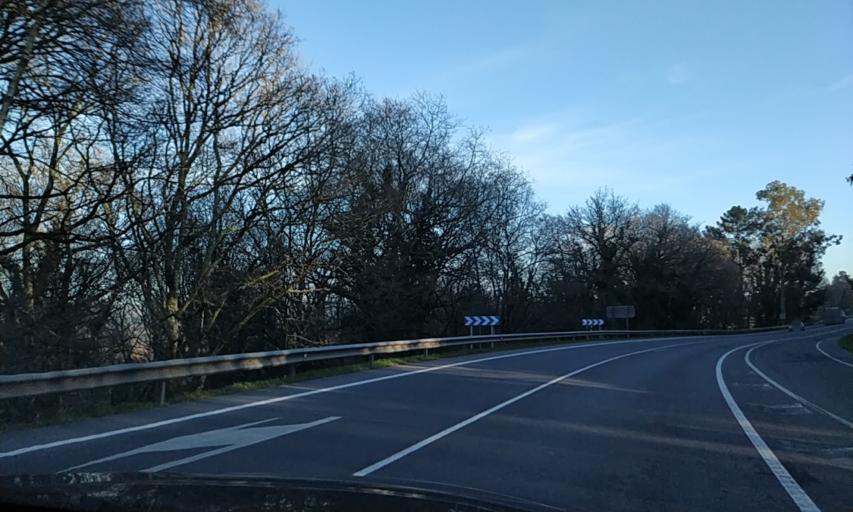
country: ES
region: Galicia
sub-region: Provincia de Pontevedra
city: Silleda
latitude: 42.6903
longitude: -8.2218
